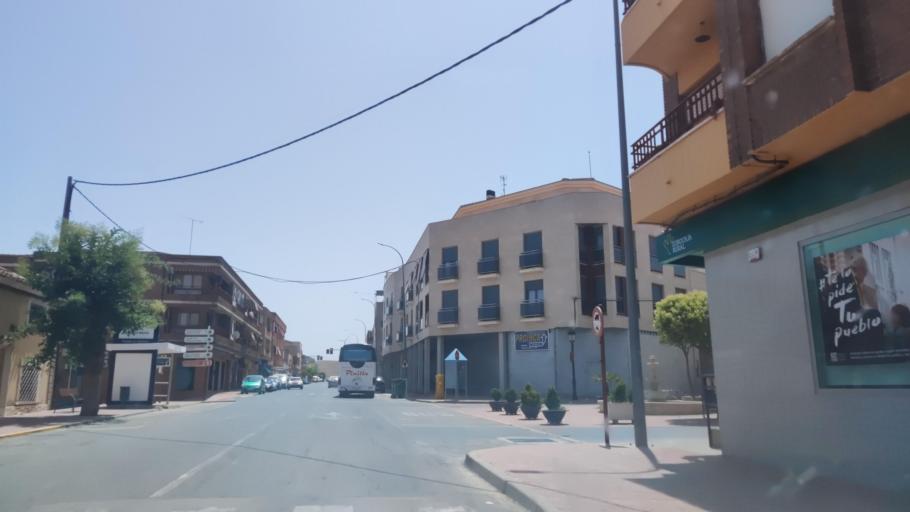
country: ES
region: Castille-La Mancha
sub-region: Provincia de Albacete
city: Pozo-Canada
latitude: 38.8041
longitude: -1.7329
